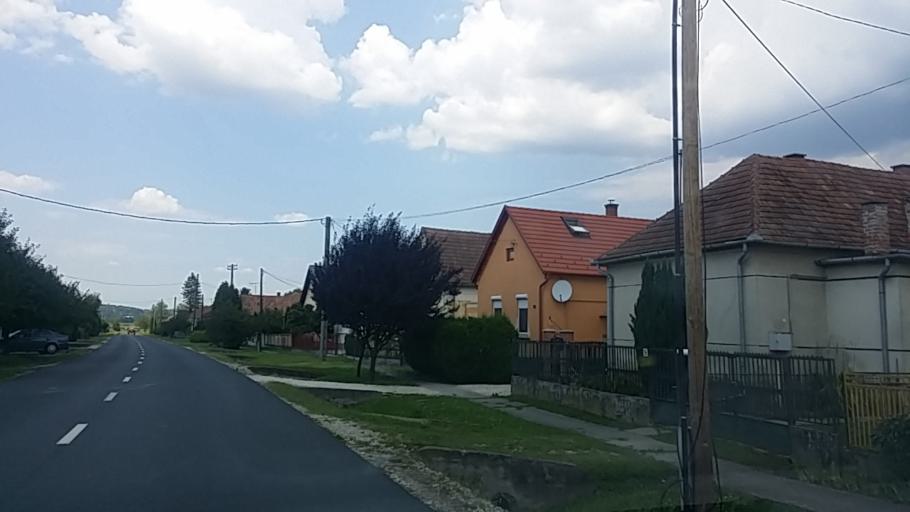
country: HR
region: Medimurska
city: Podturen
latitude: 46.5246
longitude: 16.5553
